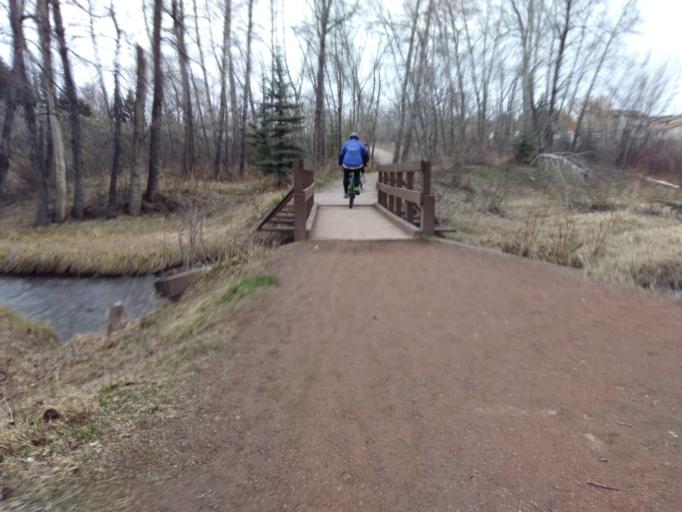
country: CA
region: Alberta
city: Cochrane
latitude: 51.1883
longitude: -114.4805
